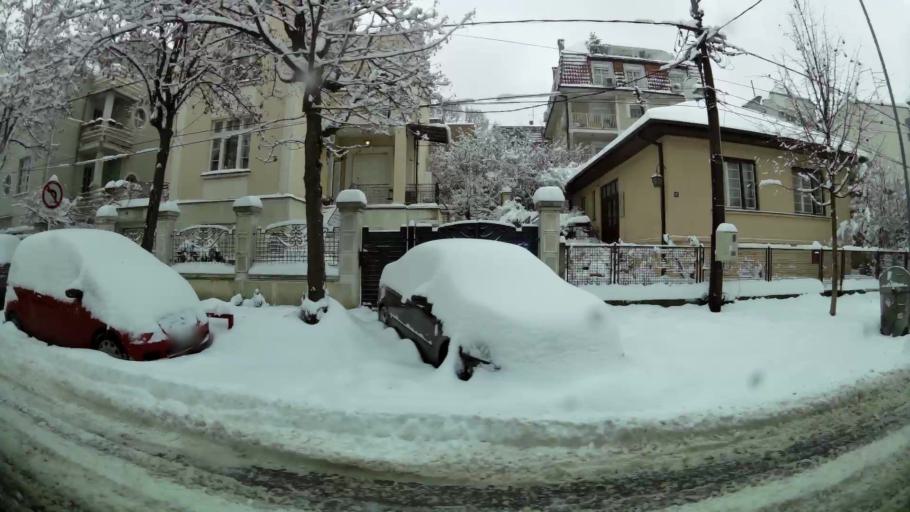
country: RS
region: Central Serbia
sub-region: Belgrade
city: Vracar
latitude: 44.7918
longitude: 20.4810
